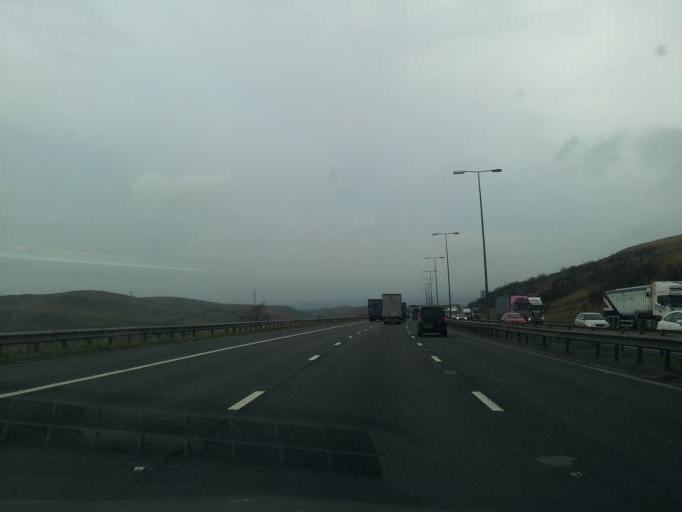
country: GB
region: England
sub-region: Borough of Rochdale
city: Littleborough
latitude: 53.6246
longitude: -2.0518
